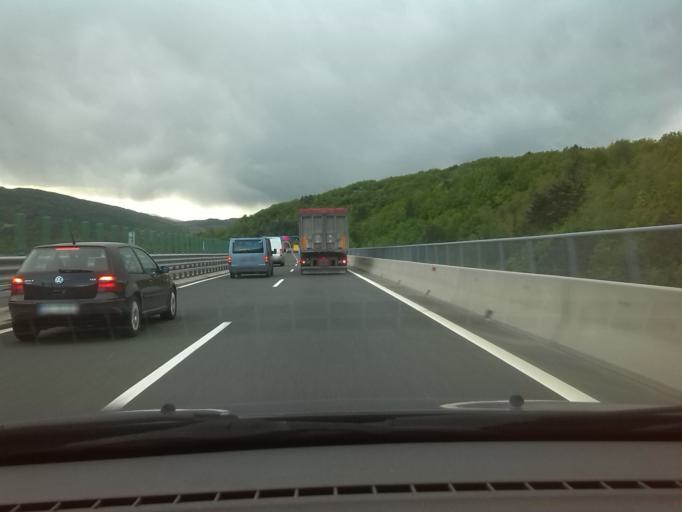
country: SI
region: Vipava
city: Vipava
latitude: 45.7906
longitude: 13.9973
